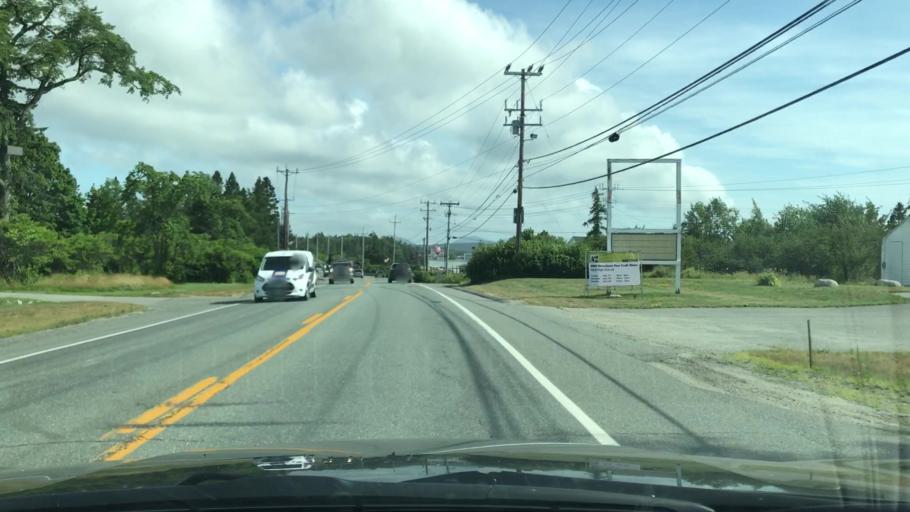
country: US
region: Maine
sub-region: Hancock County
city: Trenton
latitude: 44.4339
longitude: -68.3689
